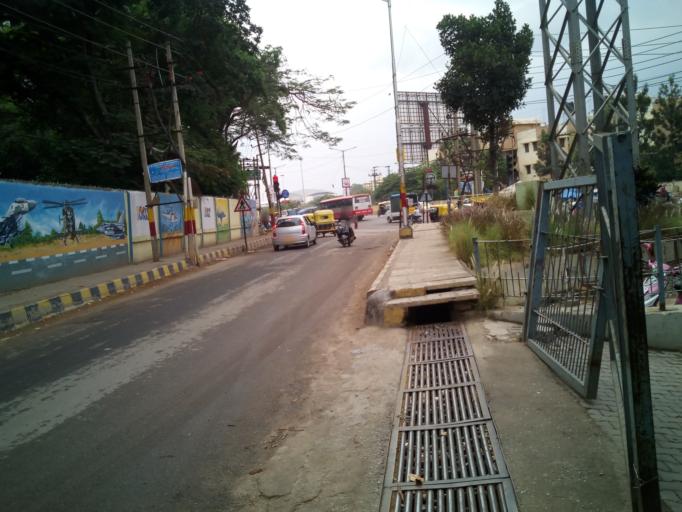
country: IN
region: Karnataka
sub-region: Bangalore Urban
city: Bangalore
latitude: 12.9911
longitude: 77.6578
